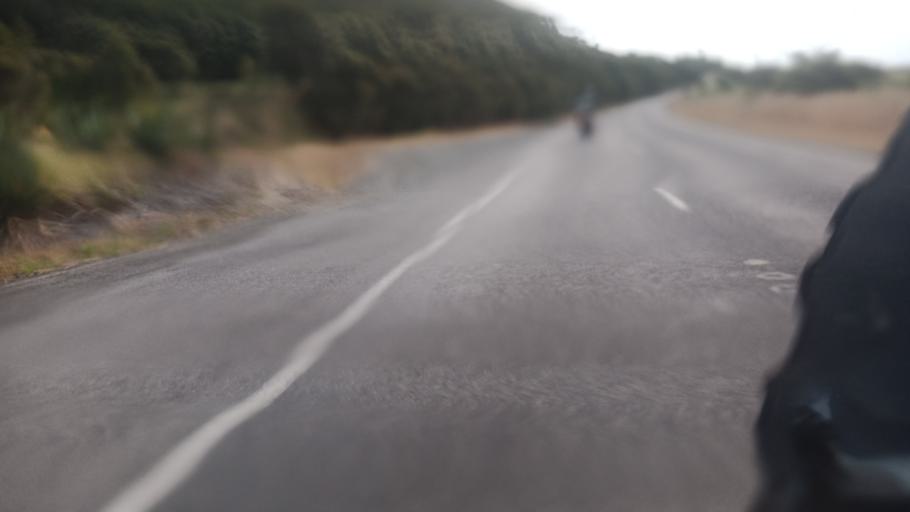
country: NZ
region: Bay of Plenty
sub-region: Opotiki District
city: Opotiki
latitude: -37.8691
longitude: 177.6000
